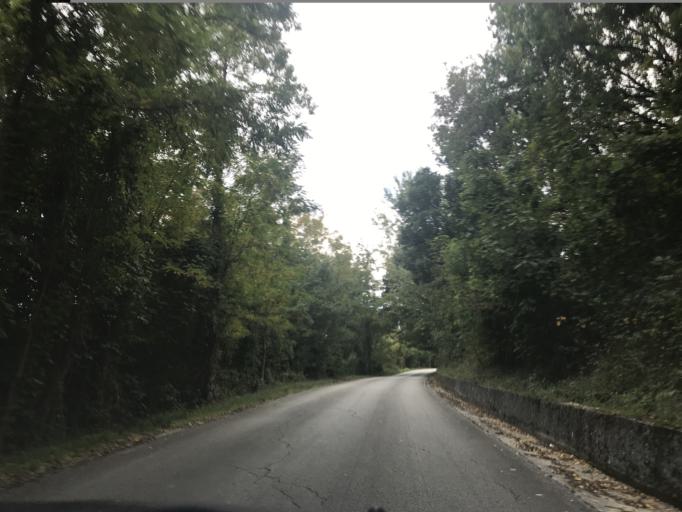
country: IT
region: Molise
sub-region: Provincia di Campobasso
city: Duronia
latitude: 41.6628
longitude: 14.4607
